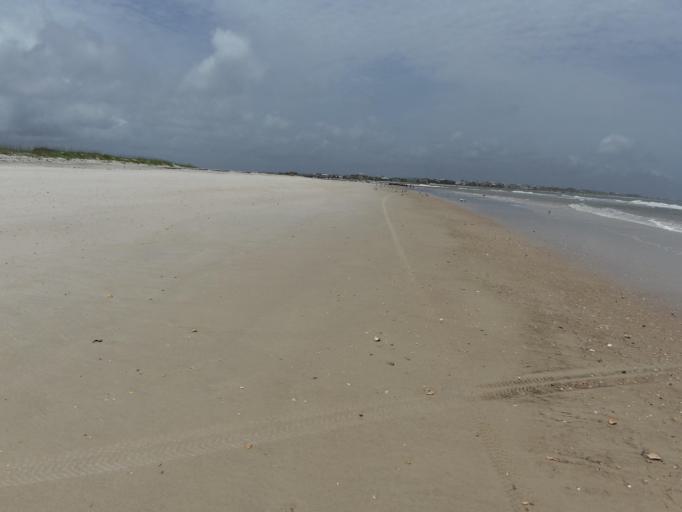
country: US
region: Florida
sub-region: Saint Johns County
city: Saint Augustine
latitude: 29.9074
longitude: -81.2814
